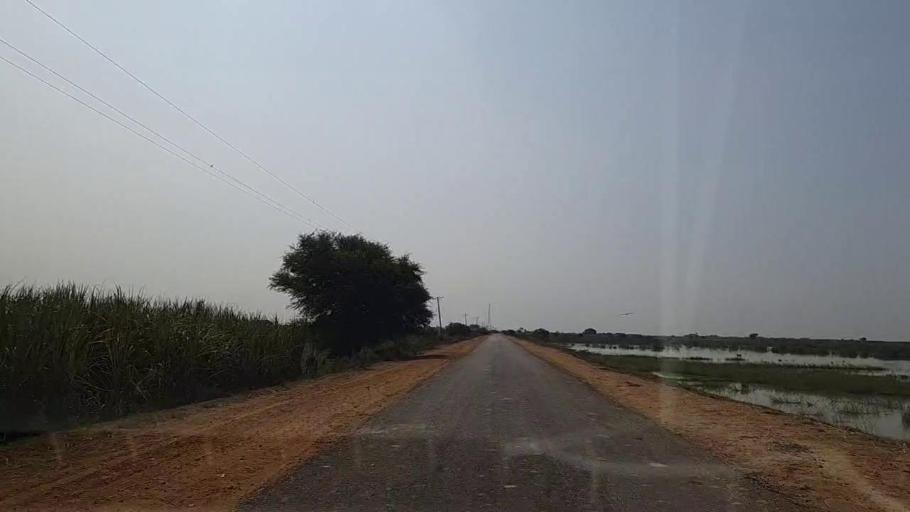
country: PK
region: Sindh
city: Chuhar Jamali
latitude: 24.2946
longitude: 67.9288
